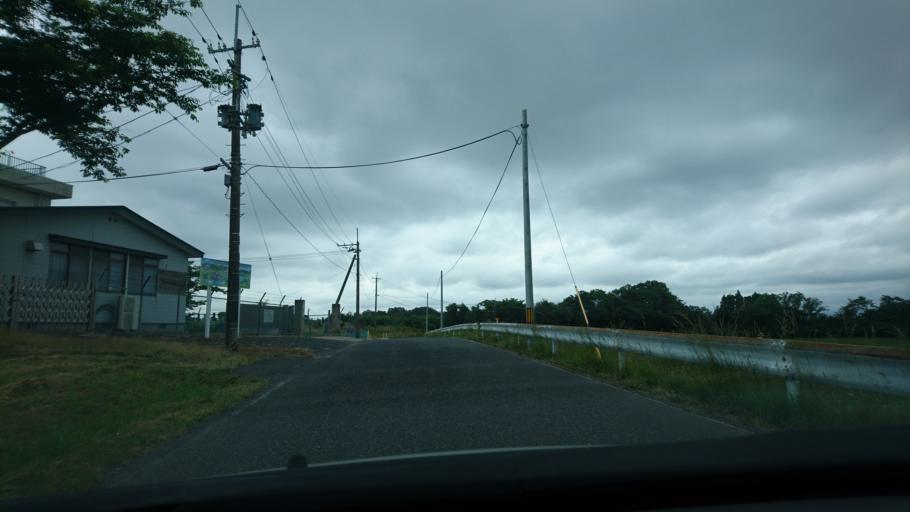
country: JP
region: Iwate
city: Ichinoseki
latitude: 38.8796
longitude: 141.2011
